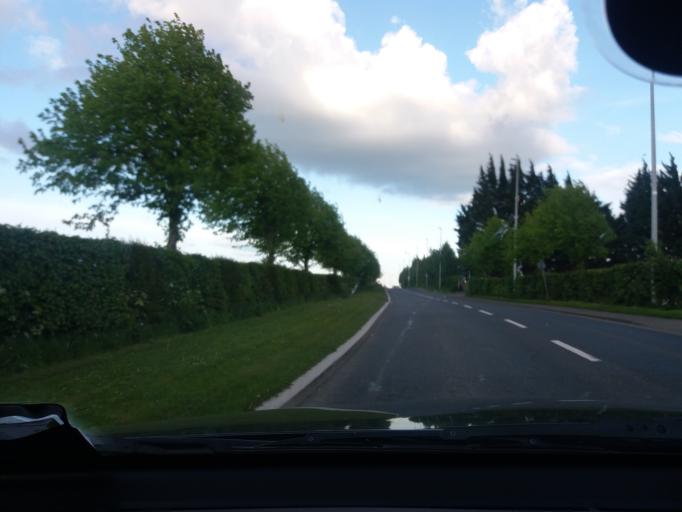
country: IE
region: Leinster
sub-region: South Dublin
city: Newcastle
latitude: 53.2946
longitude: -6.4870
